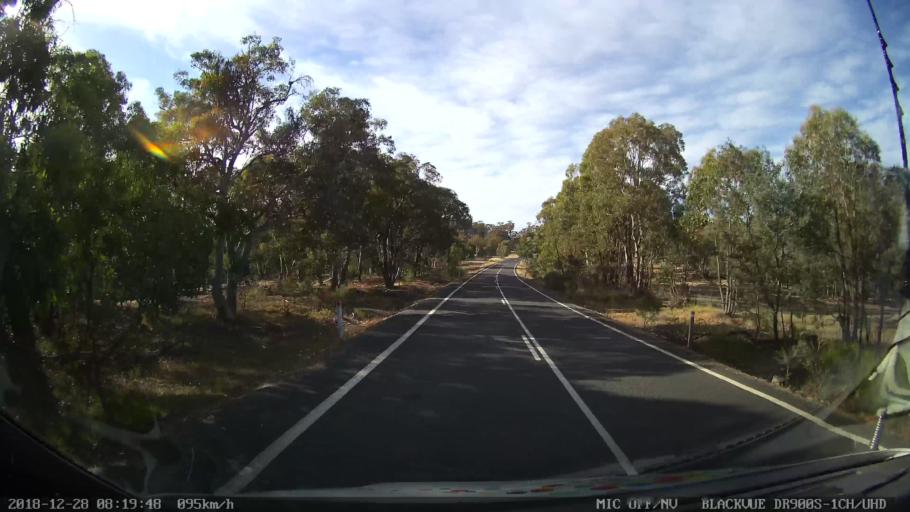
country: AU
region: New South Wales
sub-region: Blayney
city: Blayney
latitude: -33.8639
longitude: 149.3524
